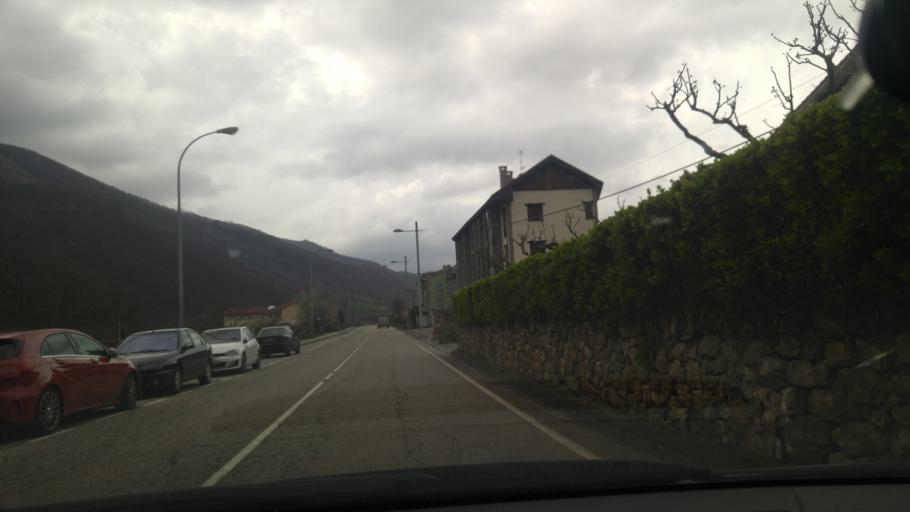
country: ES
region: Asturias
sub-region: Province of Asturias
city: Rio Aller
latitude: 43.1053
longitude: -5.5116
